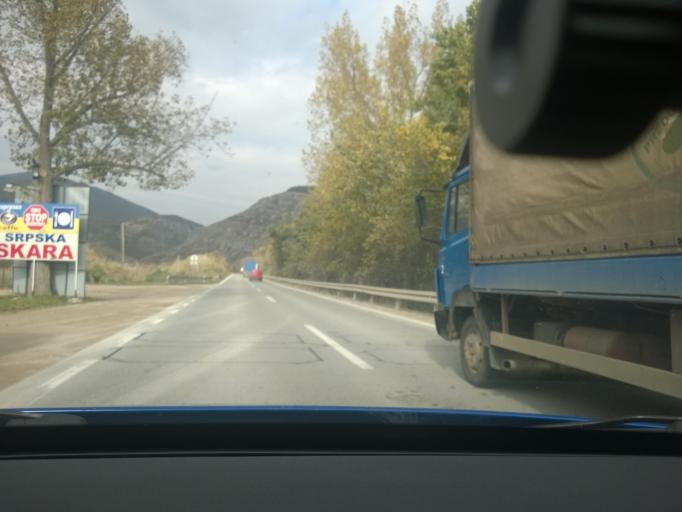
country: RS
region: Central Serbia
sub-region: Nisavski Okrug
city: Svrljig
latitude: 43.3030
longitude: 22.1938
